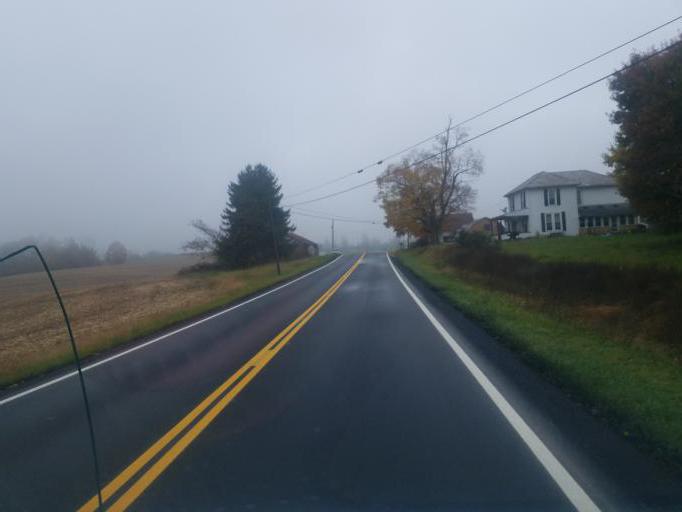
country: US
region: Ohio
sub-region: Morgan County
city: McConnelsville
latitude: 39.5651
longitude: -81.8337
